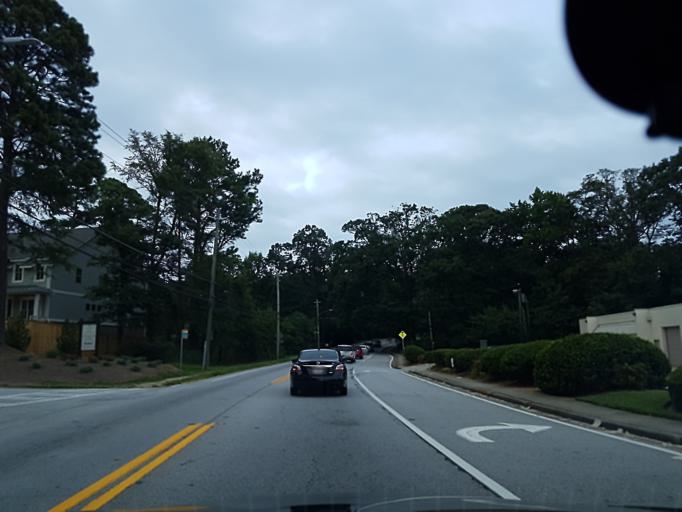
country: US
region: Georgia
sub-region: DeKalb County
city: North Druid Hills
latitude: 33.8139
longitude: -84.3339
